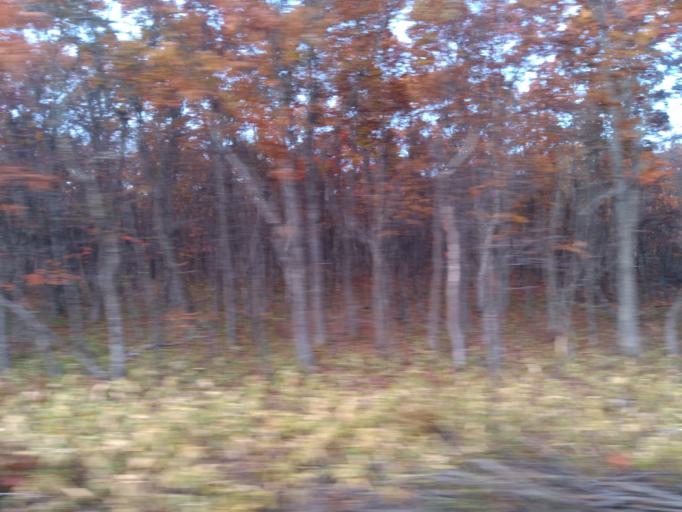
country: JP
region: Hokkaido
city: Tomakomai
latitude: 42.6896
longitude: 141.7270
